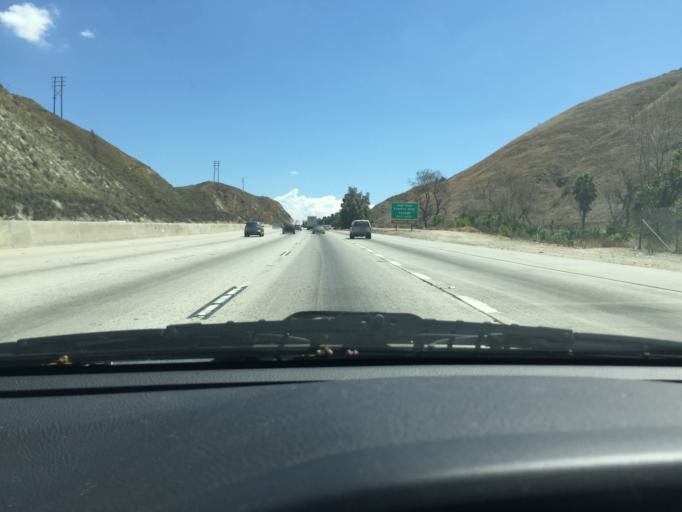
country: US
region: California
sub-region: San Bernardino County
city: Mentone
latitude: 34.0309
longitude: -117.1339
